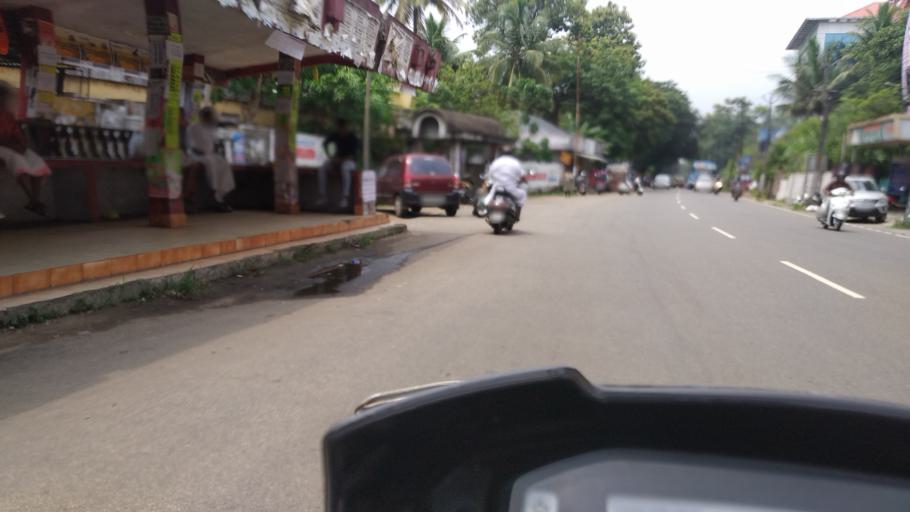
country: IN
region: Kerala
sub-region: Ernakulam
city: Perumpavur
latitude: 10.1155
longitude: 76.4815
